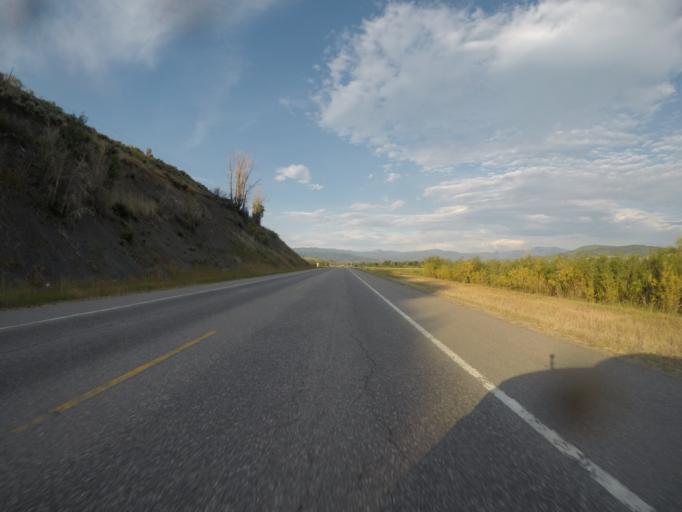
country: US
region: Colorado
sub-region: Routt County
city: Steamboat Springs
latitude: 40.4899
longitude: -106.9602
